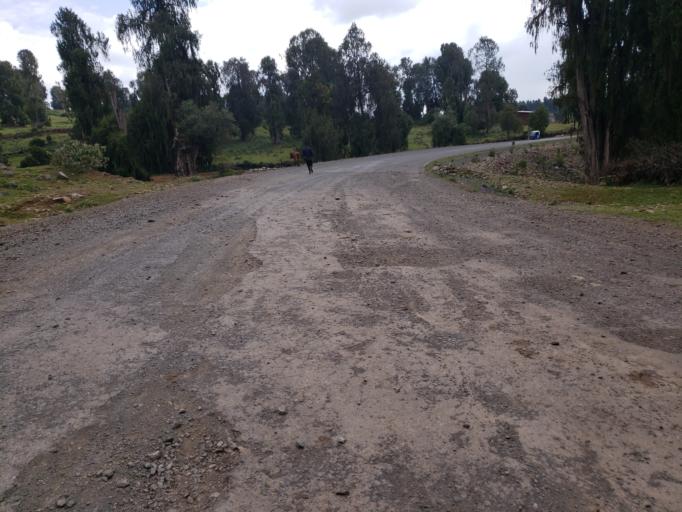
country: ET
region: Oromiya
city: Dodola
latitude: 6.8884
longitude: 39.3897
